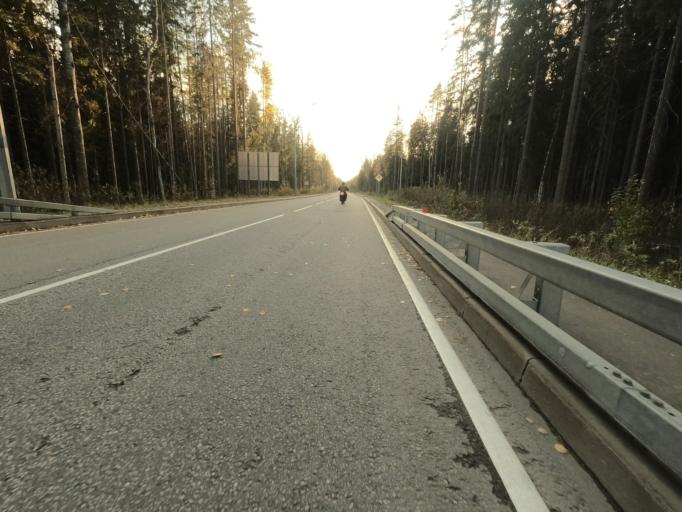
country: RU
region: St.-Petersburg
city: Solnechnoye
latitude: 60.1679
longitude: 29.9660
